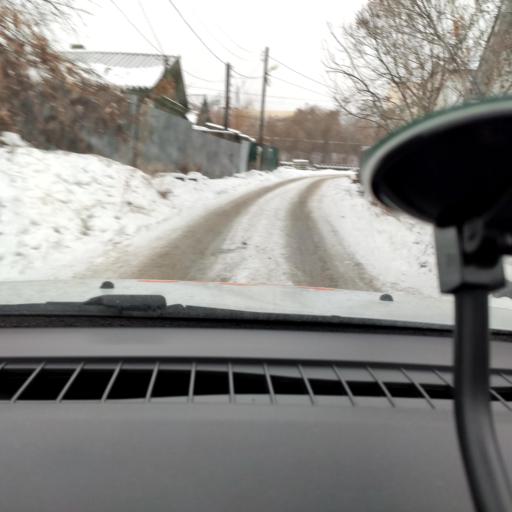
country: RU
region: Samara
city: Samara
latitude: 53.1838
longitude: 50.1131
